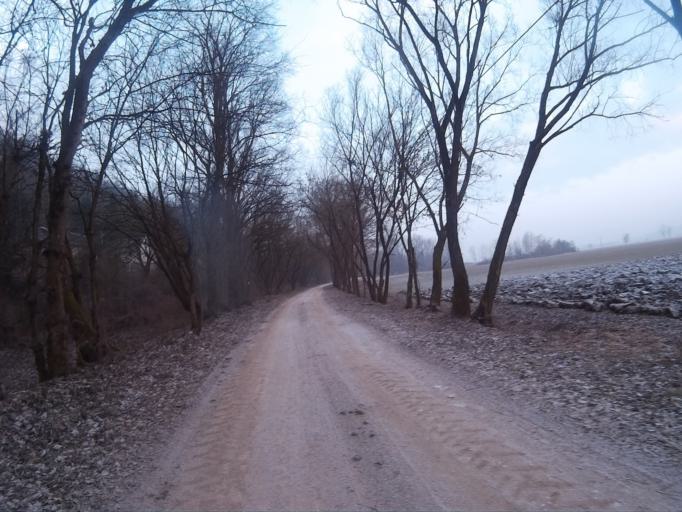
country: HU
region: Borsod-Abauj-Zemplen
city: Szendro
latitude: 48.5175
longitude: 20.7414
